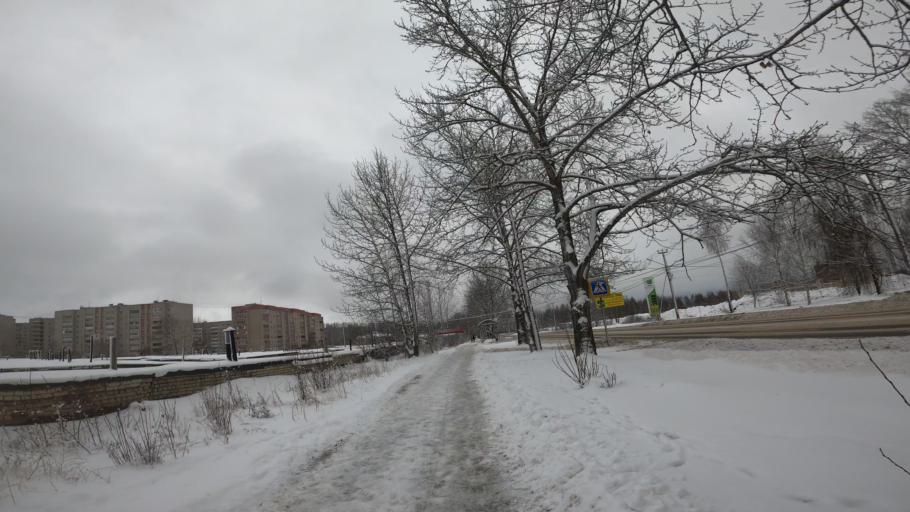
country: RU
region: Jaroslavl
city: Pereslavl'-Zalesskiy
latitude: 56.7486
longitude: 38.8871
